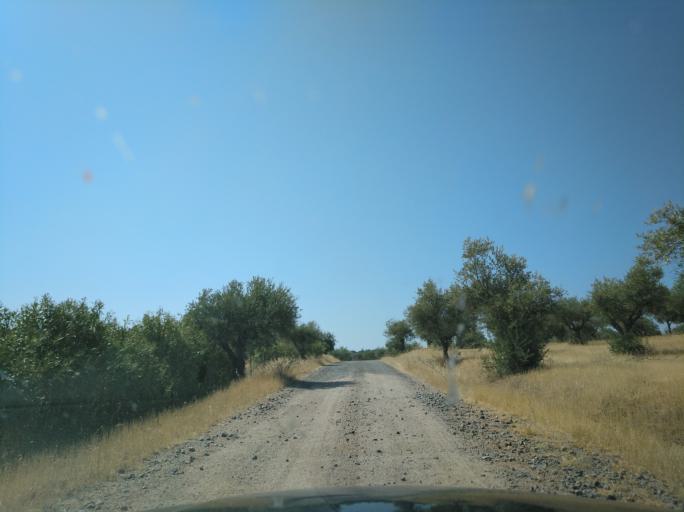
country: PT
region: Portalegre
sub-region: Campo Maior
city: Campo Maior
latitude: 39.0719
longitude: -7.0170
